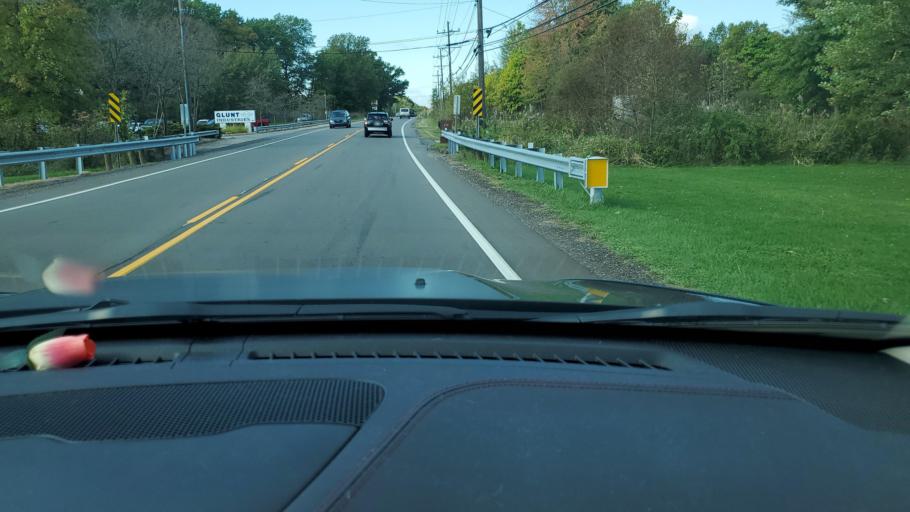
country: US
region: Ohio
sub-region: Trumbull County
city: Warren
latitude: 41.2656
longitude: -80.8176
